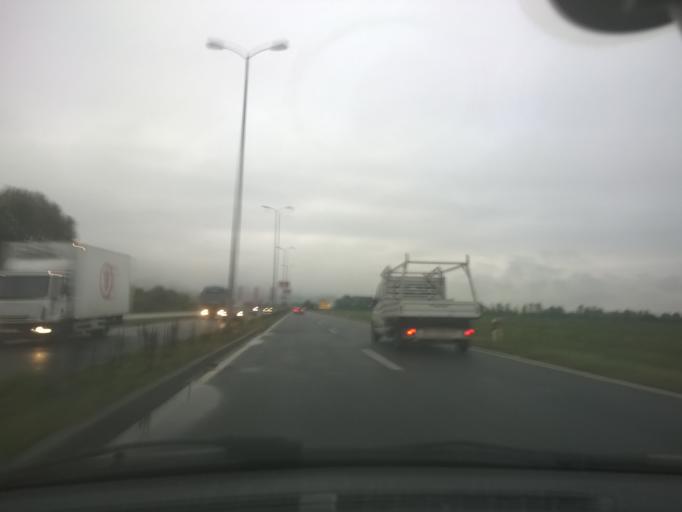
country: HR
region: Zagrebacka
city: Zapresic
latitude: 45.8748
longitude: 15.8199
